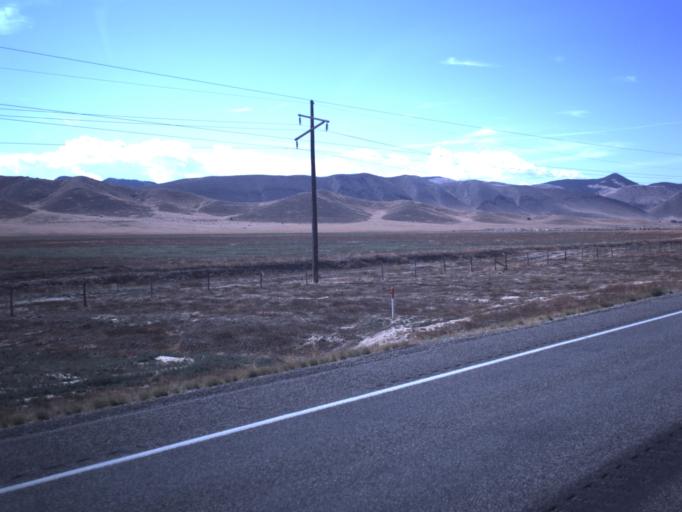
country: US
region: Utah
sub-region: Sevier County
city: Salina
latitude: 39.0260
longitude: -111.8313
